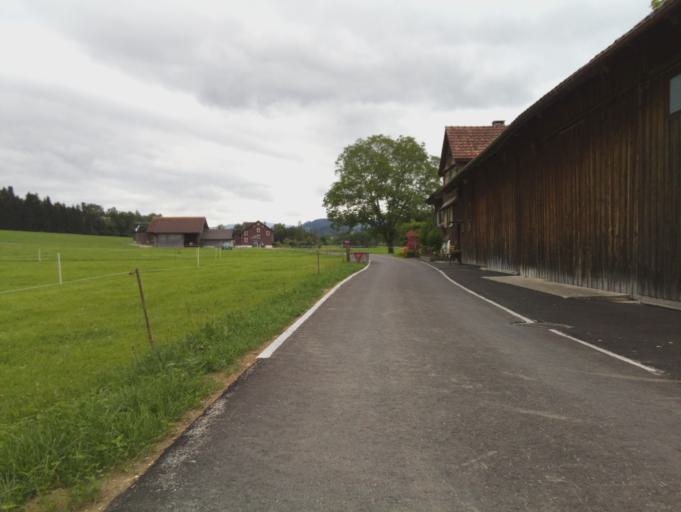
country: CH
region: Saint Gallen
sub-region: Wahlkreis Toggenburg
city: Buetschwil
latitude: 47.3650
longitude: 9.0816
